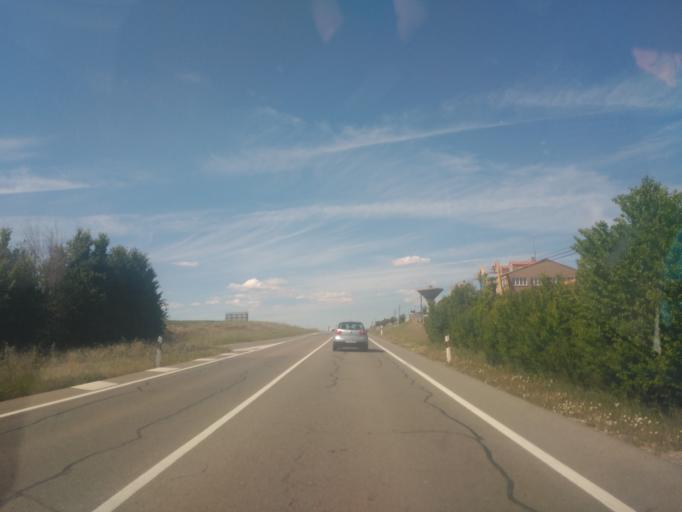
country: ES
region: Castille and Leon
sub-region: Provincia de Salamanca
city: Carbajosa de la Sagrada
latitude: 40.9276
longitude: -5.6685
